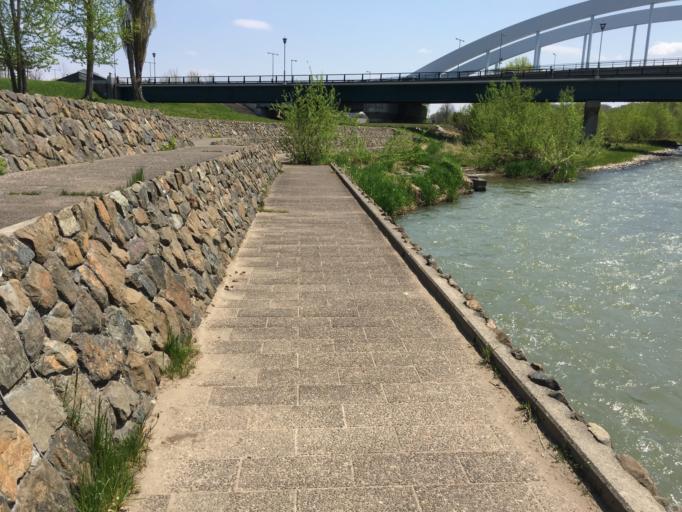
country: JP
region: Hokkaido
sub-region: Asahikawa-shi
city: Asahikawa
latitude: 43.7559
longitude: 142.3658
